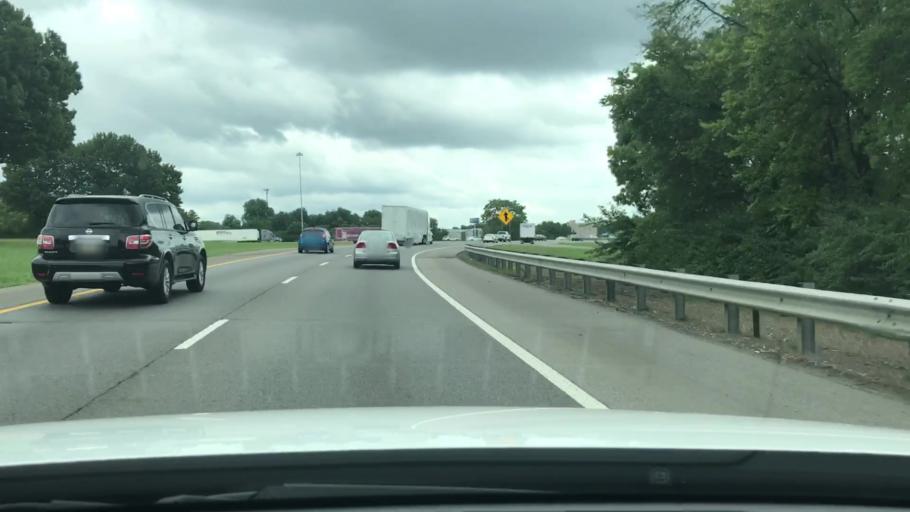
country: US
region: Tennessee
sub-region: Davidson County
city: Nashville
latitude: 36.1395
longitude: -86.7295
